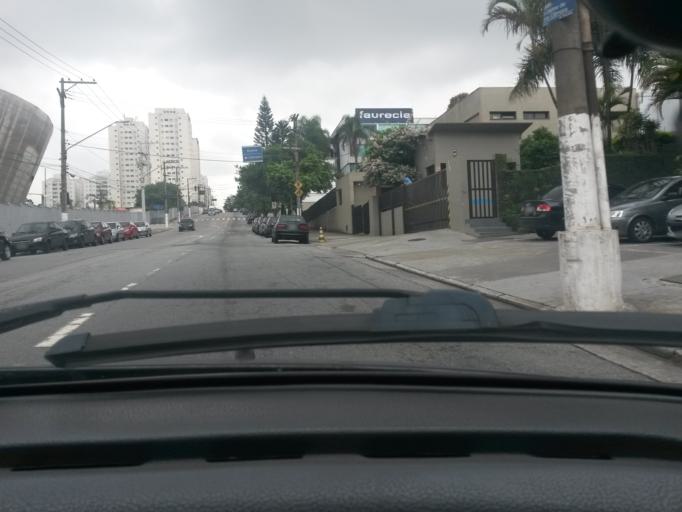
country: BR
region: Sao Paulo
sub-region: Sao Bernardo Do Campo
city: Sao Bernardo do Campo
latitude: -23.7072
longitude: -46.5628
